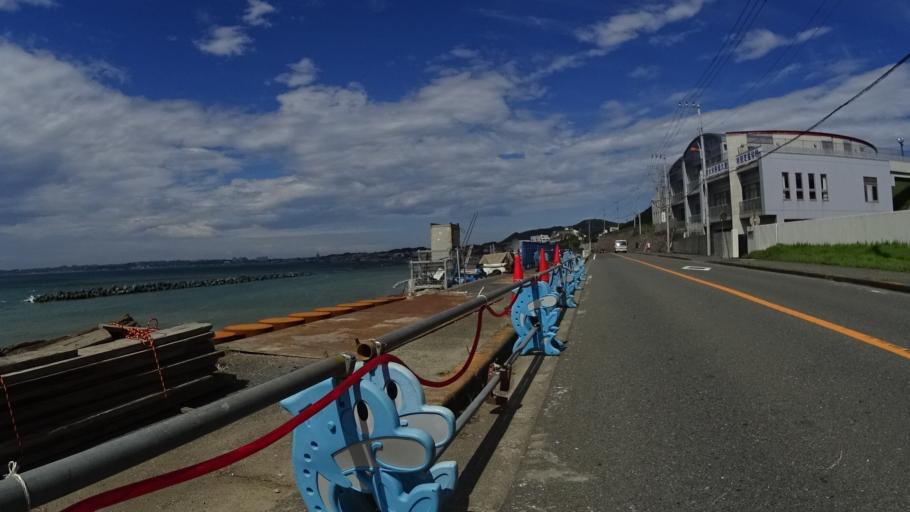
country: JP
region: Kanagawa
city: Yokosuka
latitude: 35.2104
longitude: 139.7000
